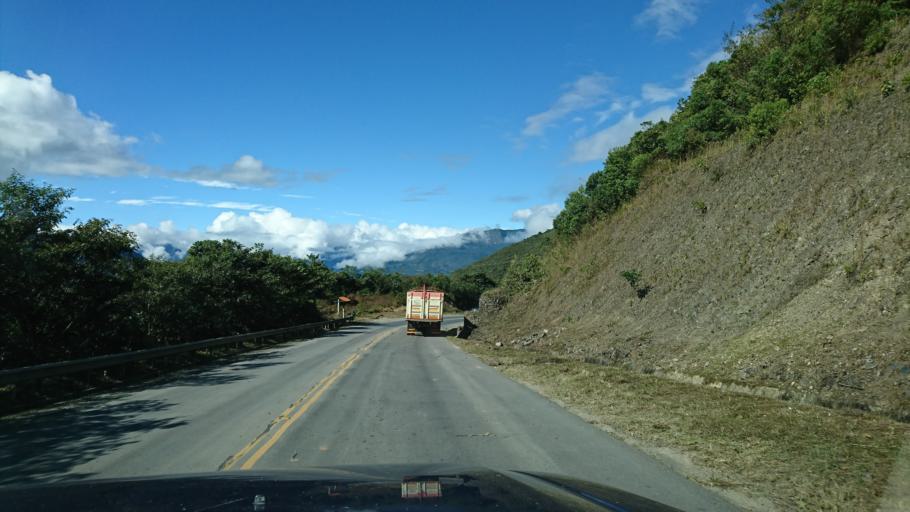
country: BO
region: La Paz
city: Coroico
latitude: -16.2128
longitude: -67.8168
